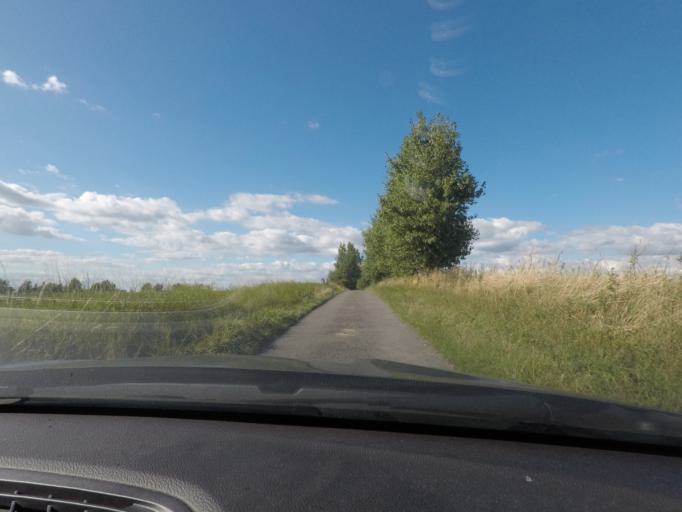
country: DK
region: Zealand
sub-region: Guldborgsund Kommune
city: Sakskobing
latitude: 54.9598
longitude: 11.5389
